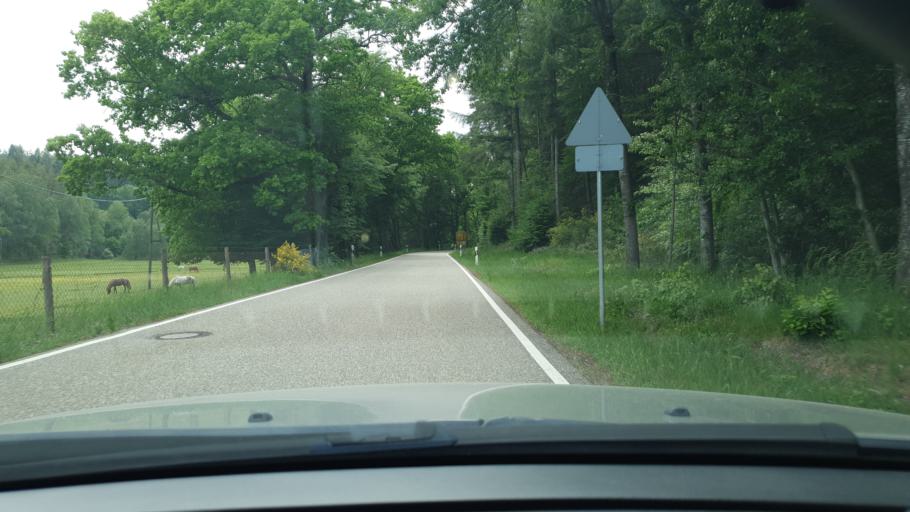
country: DE
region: Rheinland-Pfalz
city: Stelzenberg
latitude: 49.3954
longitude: 7.7650
